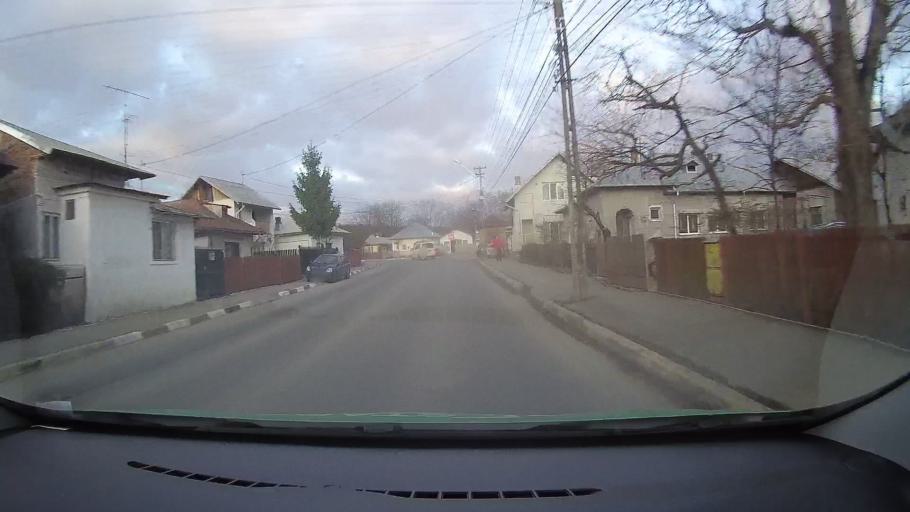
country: RO
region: Dambovita
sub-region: Municipiul Moreni
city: Moreni
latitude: 44.9950
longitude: 25.6475
